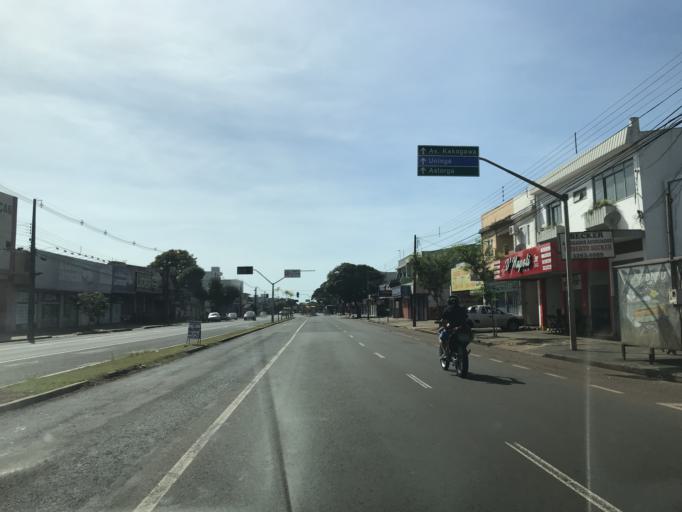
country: BR
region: Parana
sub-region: Maringa
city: Maringa
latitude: -23.4030
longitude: -51.9284
